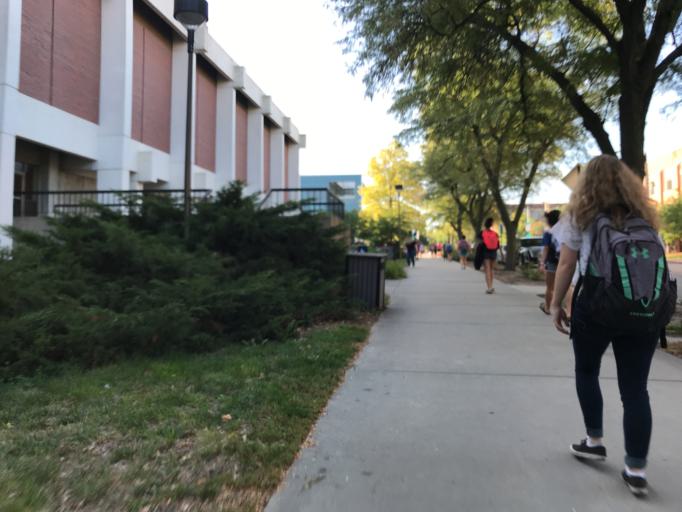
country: US
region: Nebraska
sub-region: Lancaster County
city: Lincoln
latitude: 40.8219
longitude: -96.7011
